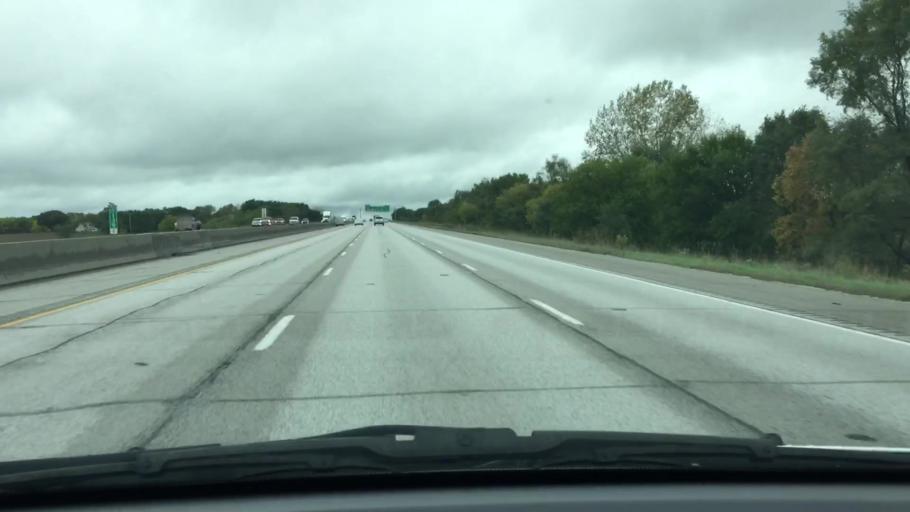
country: US
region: Iowa
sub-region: Polk County
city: Pleasant Hill
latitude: 41.6556
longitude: -93.5524
